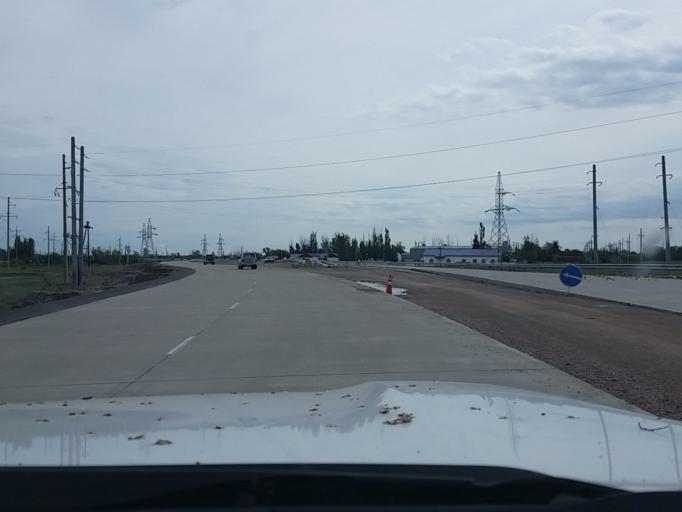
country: KZ
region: Almaty Oblysy
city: Turgen'
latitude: 43.5832
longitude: 78.2672
